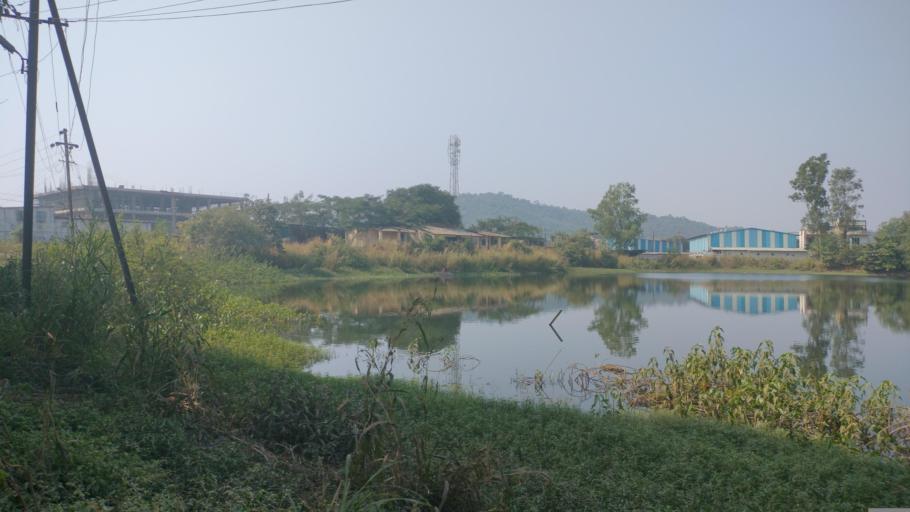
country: IN
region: Maharashtra
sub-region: Thane
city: Bhayandar
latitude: 19.3536
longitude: 72.9113
